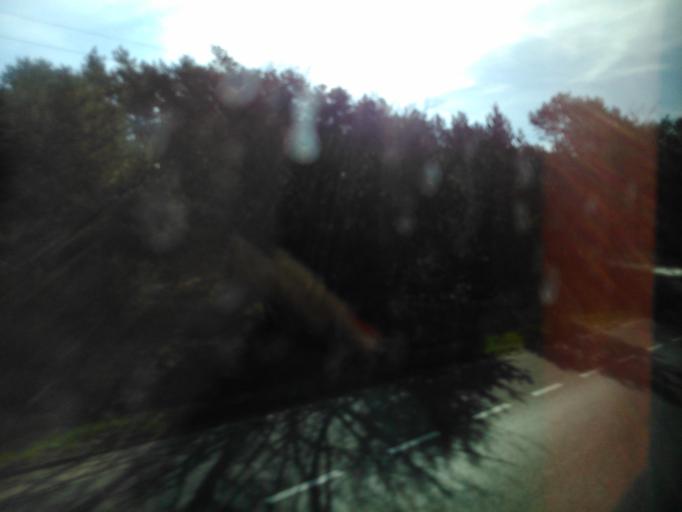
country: PL
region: Kujawsko-Pomorskie
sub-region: Torun
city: Torun
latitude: 52.9773
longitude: 18.6748
